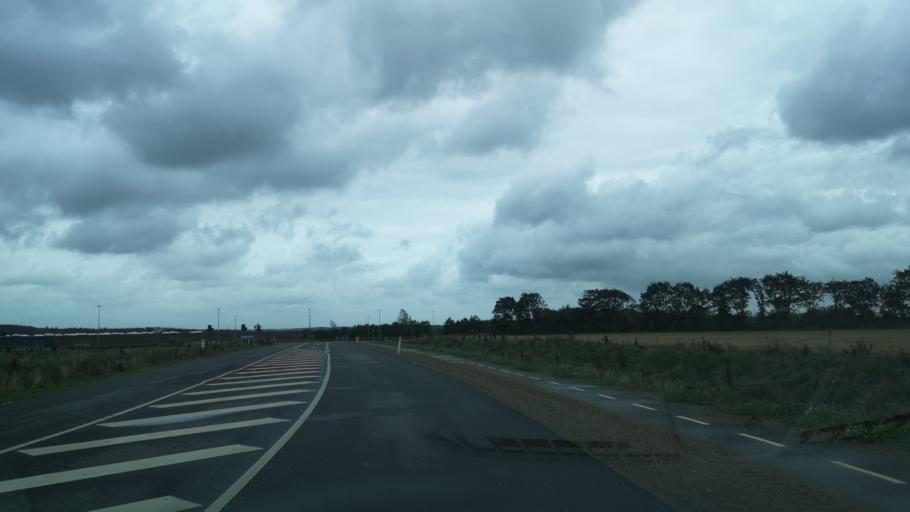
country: DK
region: Central Jutland
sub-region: Ringkobing-Skjern Kommune
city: Videbaek
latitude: 56.0462
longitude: 8.6698
